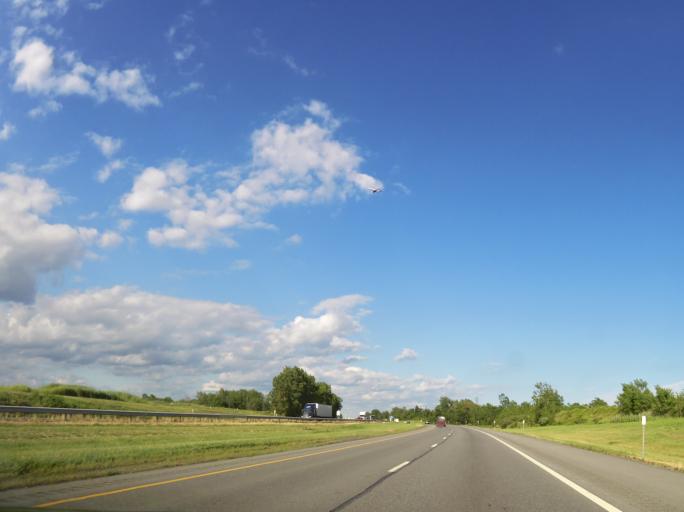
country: US
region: New York
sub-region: Erie County
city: Clarence
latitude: 42.9499
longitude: -78.6117
